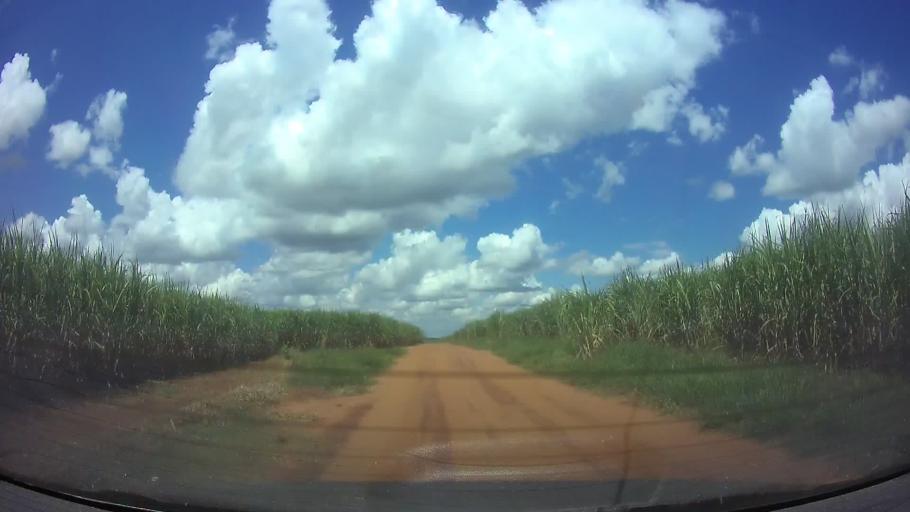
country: PY
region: Paraguari
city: La Colmena
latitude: -25.9647
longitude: -56.7580
